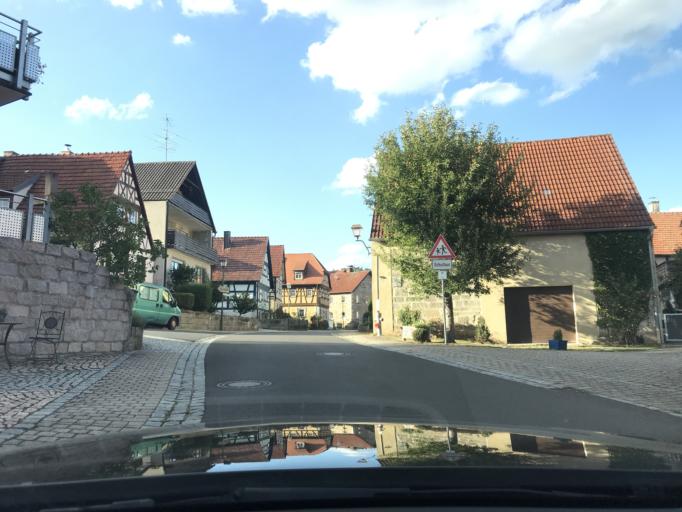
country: DE
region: Bavaria
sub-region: Regierungsbezirk Unterfranken
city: Breitbrunn
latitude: 50.0351
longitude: 10.6897
